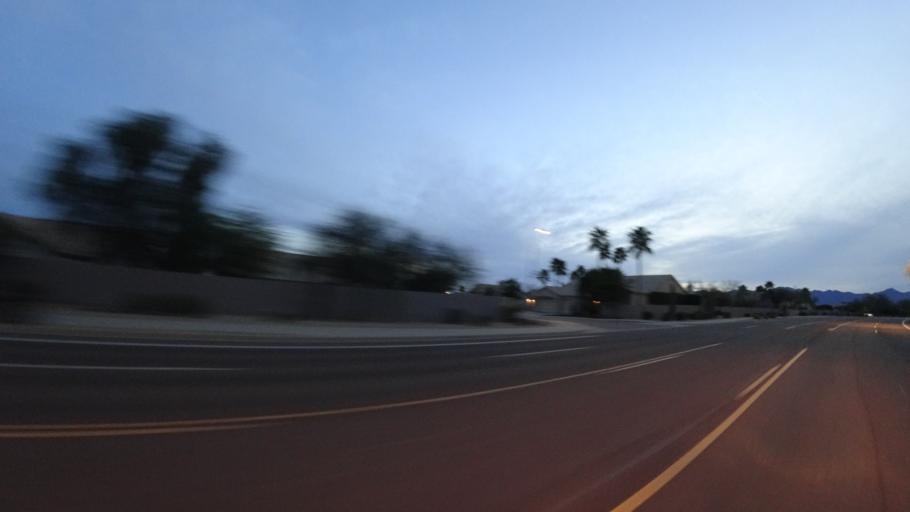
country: US
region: Arizona
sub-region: Maricopa County
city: Laveen
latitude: 33.3039
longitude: -112.0830
